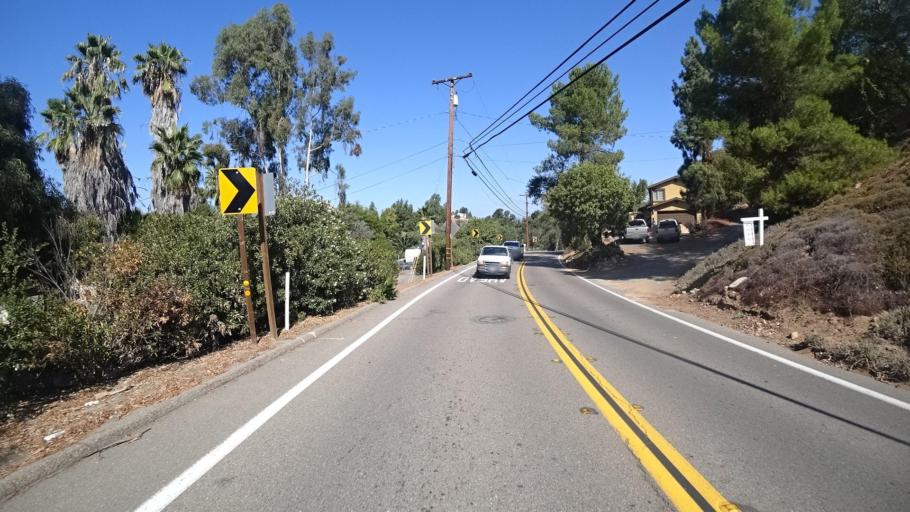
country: US
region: California
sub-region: San Diego County
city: Winter Gardens
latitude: 32.8467
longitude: -116.9421
